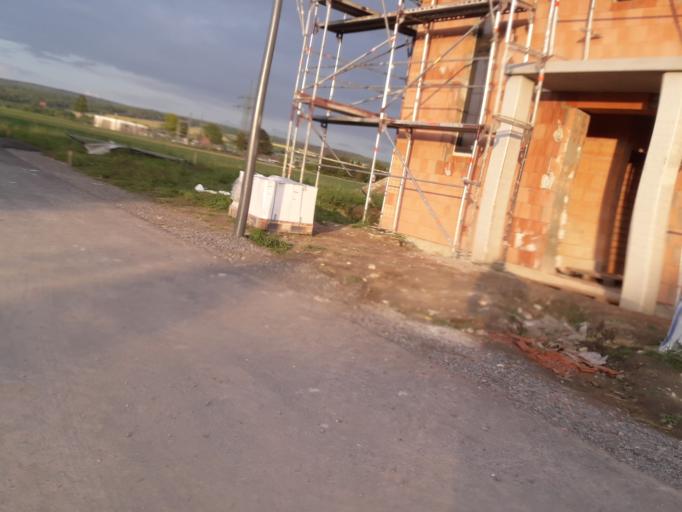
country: DE
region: North Rhine-Westphalia
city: Bad Lippspringe
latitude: 51.7878
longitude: 8.8305
